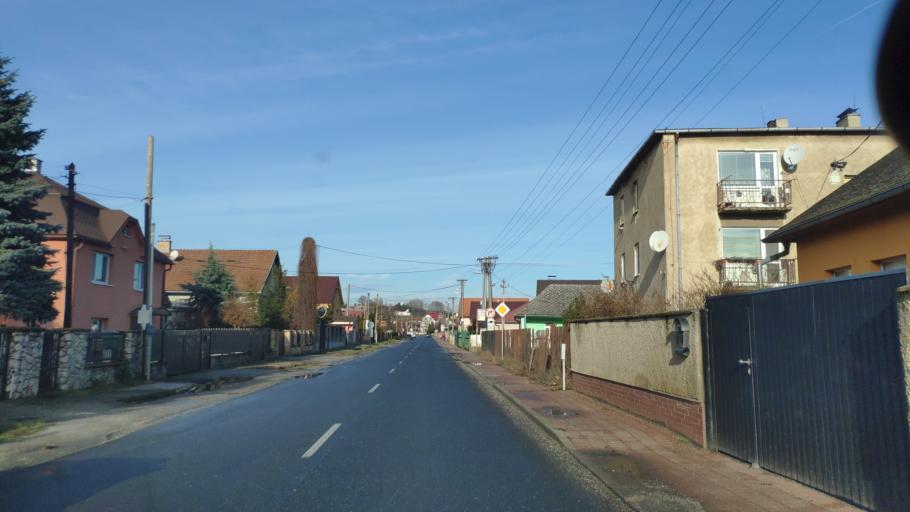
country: SK
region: Kosicky
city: Kosice
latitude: 48.6700
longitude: 21.3214
